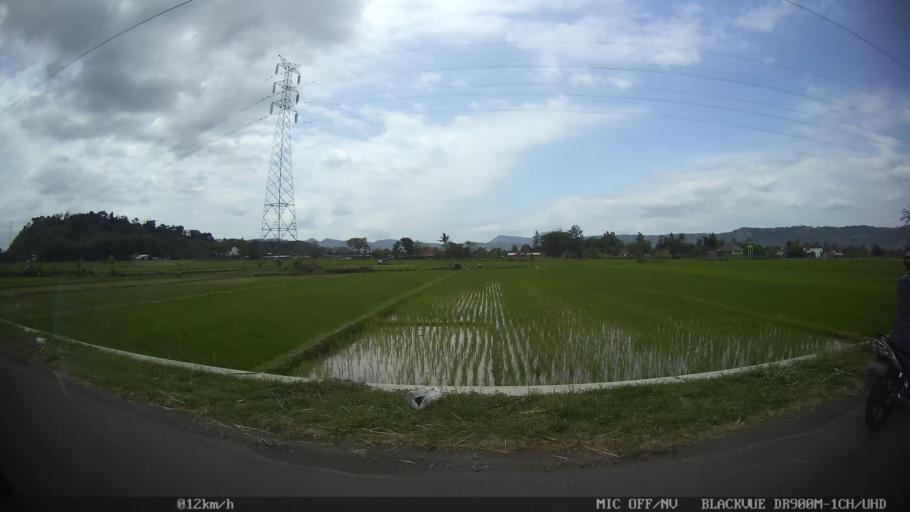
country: ID
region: Daerah Istimewa Yogyakarta
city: Depok
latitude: -7.8143
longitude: 110.4653
